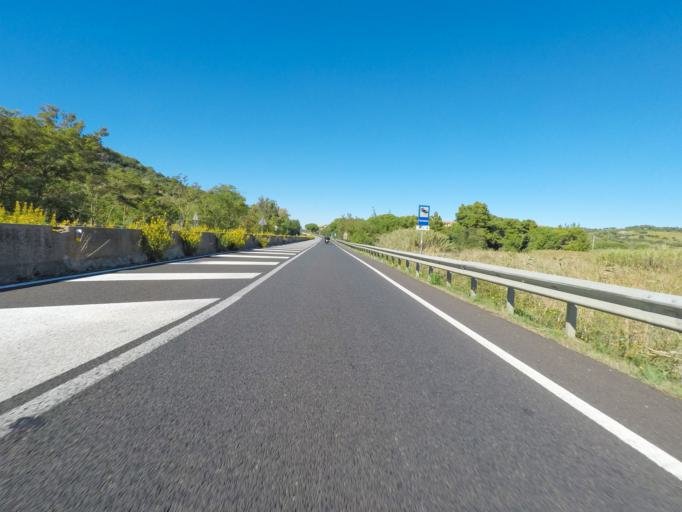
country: IT
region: Tuscany
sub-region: Provincia di Grosseto
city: Fonteblanda
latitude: 42.5495
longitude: 11.1744
